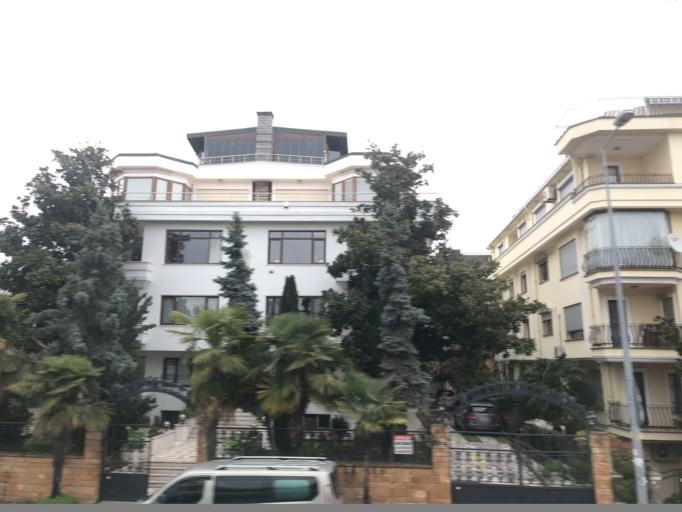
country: TR
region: Istanbul
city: Bahcelievler
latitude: 40.9691
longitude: 28.7960
